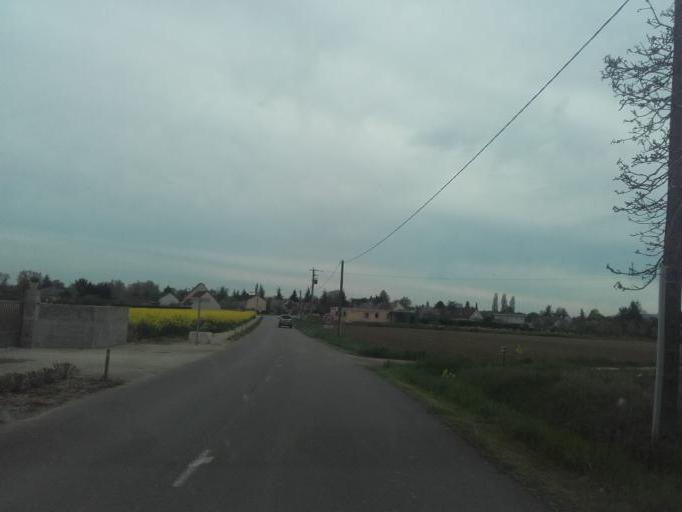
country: FR
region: Bourgogne
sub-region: Departement de Saone-et-Loire
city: Demigny
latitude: 46.9522
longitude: 4.8485
